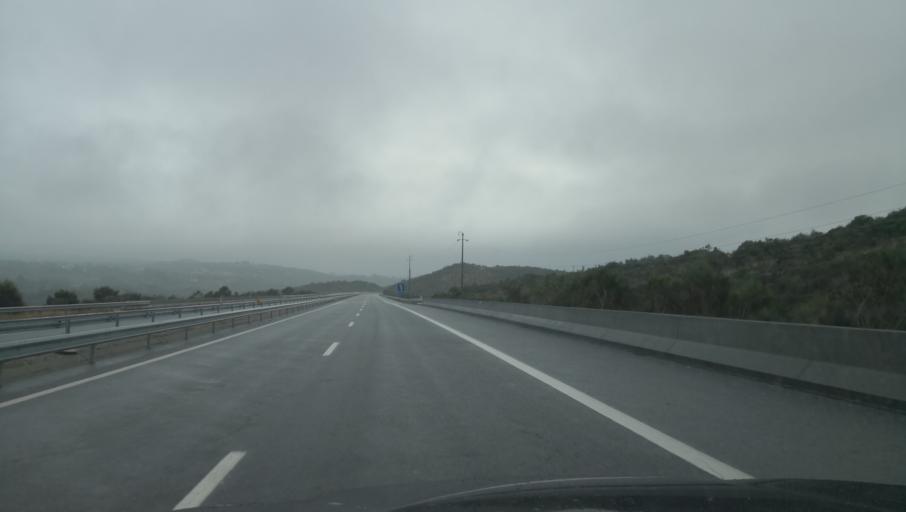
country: PT
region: Vila Real
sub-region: Vila Real
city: Vila Real
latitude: 41.3816
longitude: -7.6657
